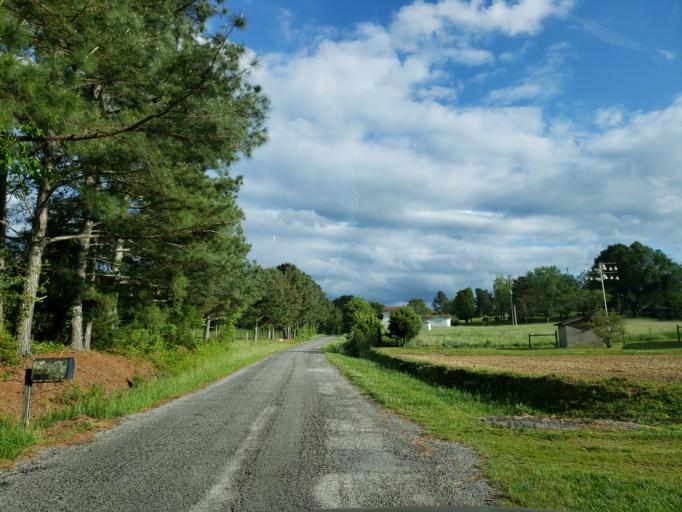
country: US
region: Georgia
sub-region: Haralson County
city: Tallapoosa
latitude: 33.8160
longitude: -85.2914
